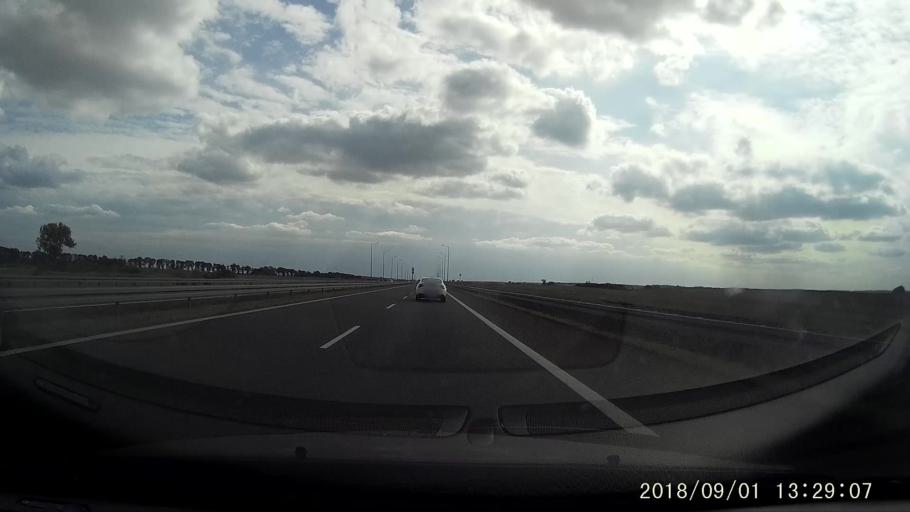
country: PL
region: West Pomeranian Voivodeship
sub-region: Powiat pyrzycki
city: Kozielice
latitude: 53.0605
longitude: 14.8635
